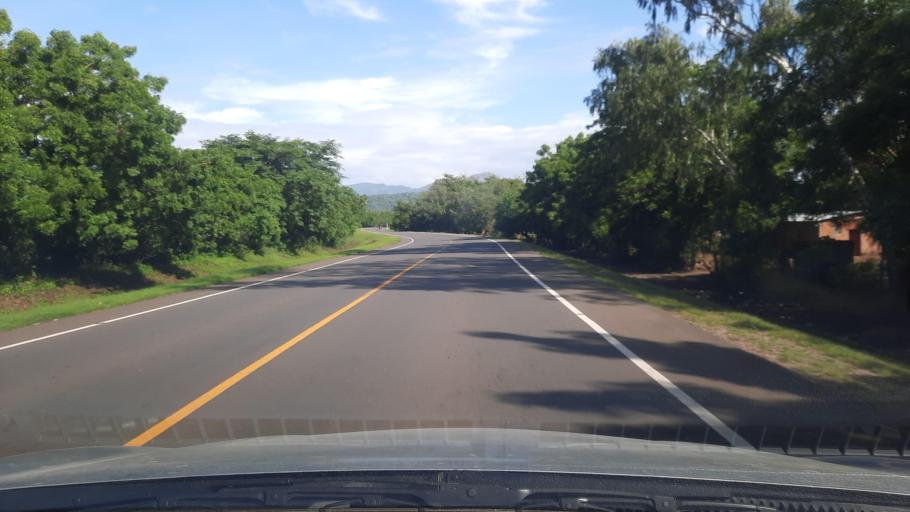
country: NI
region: Leon
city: Telica
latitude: 12.7209
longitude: -86.8774
